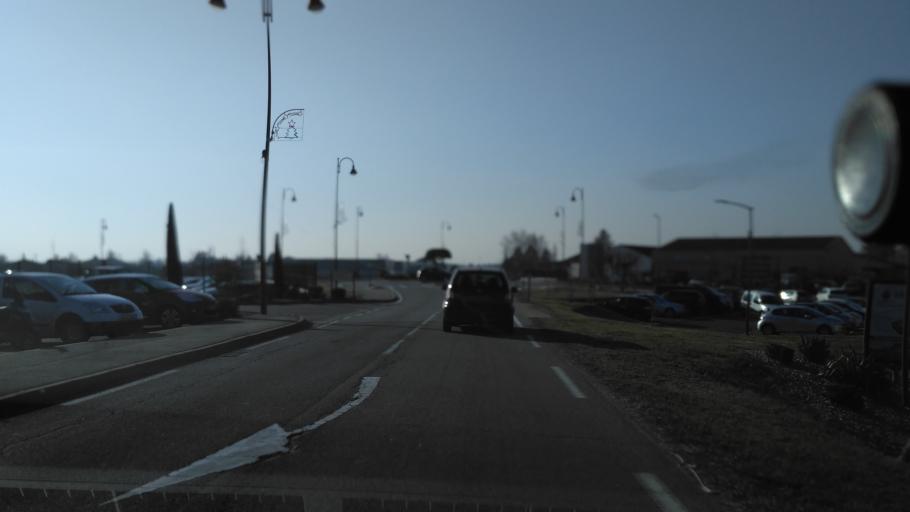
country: FR
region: Rhone-Alpes
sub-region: Departement de la Drome
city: Genissieux
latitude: 45.0806
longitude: 5.0863
